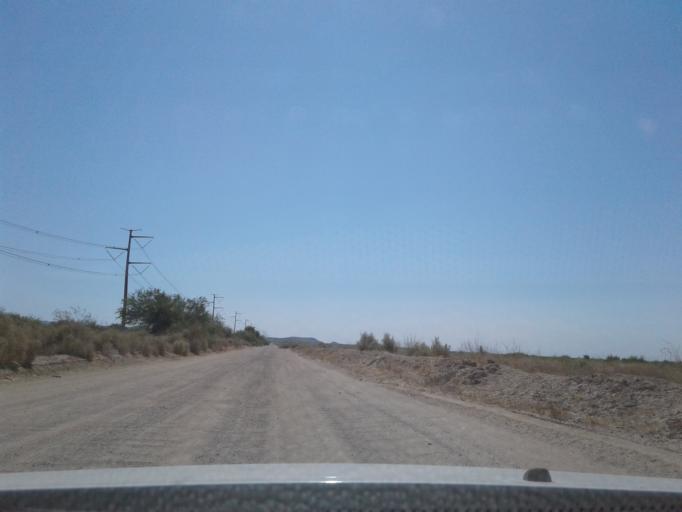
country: US
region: Arizona
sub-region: Maricopa County
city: Laveen
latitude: 33.2901
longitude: -112.1322
